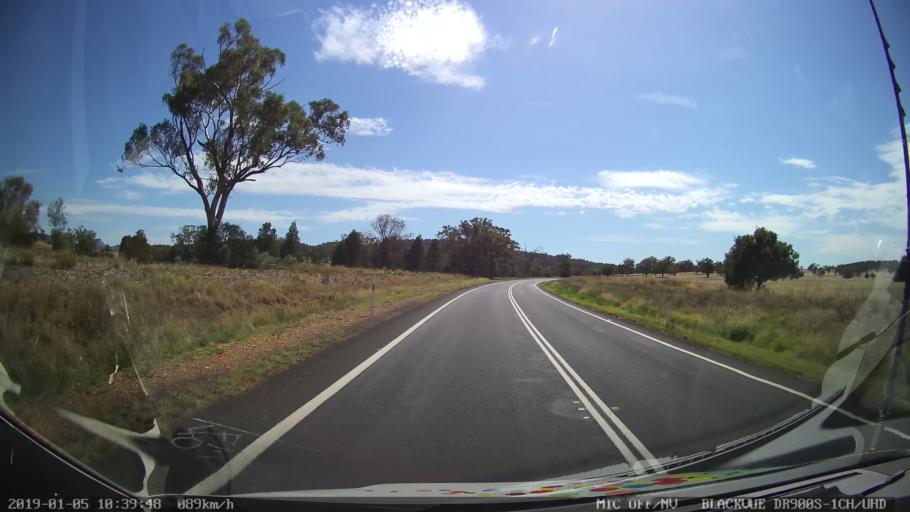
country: AU
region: New South Wales
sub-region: Gilgandra
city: Gilgandra
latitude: -31.4665
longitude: 148.9351
